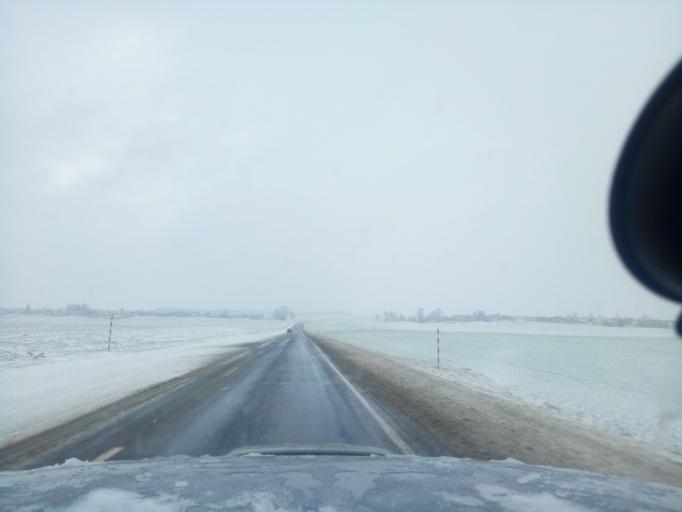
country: BY
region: Minsk
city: Haradzyeya
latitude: 53.3087
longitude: 26.5689
